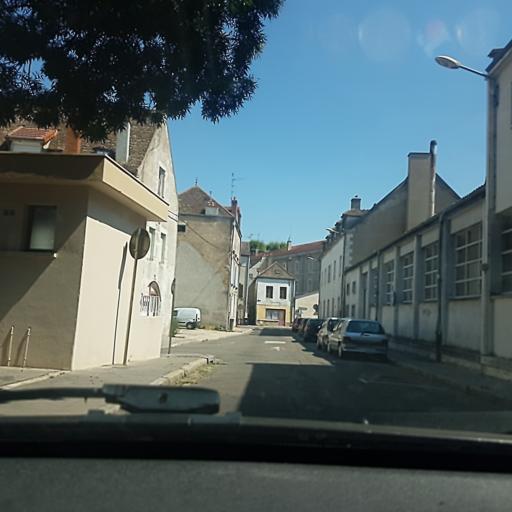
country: FR
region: Bourgogne
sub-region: Departement de Saone-et-Loire
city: Chalon-sur-Saone
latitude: 46.7792
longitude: 4.8598
